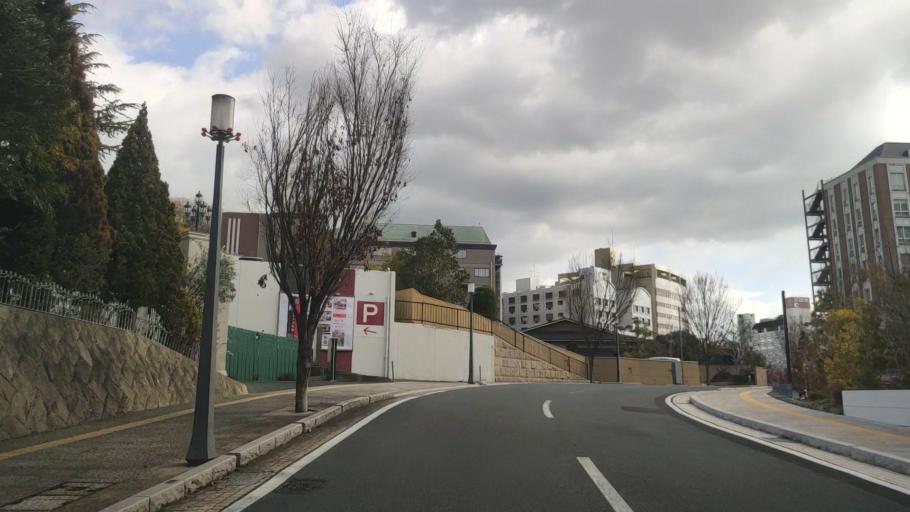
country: JP
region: Ehime
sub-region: Shikoku-chuo Shi
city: Matsuyama
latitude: 33.8541
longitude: 132.7852
